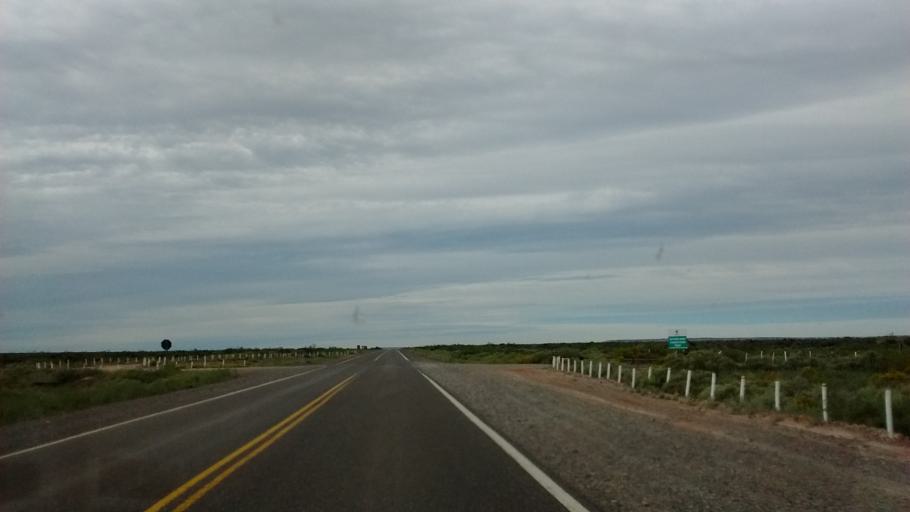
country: AR
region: Rio Negro
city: Catriel
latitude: -38.0526
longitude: -67.9200
